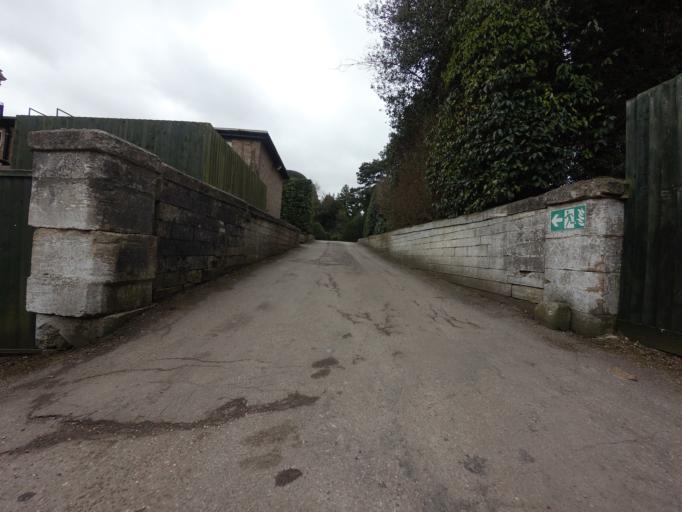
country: GB
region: England
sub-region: Lincolnshire
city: Grantham
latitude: 52.8425
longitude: -0.6386
